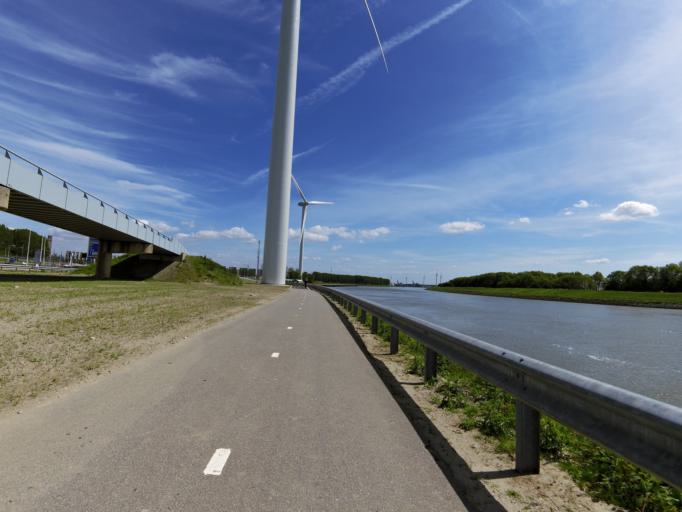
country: NL
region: South Holland
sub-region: Gemeente Maassluis
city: Maassluis
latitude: 51.9011
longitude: 4.2149
